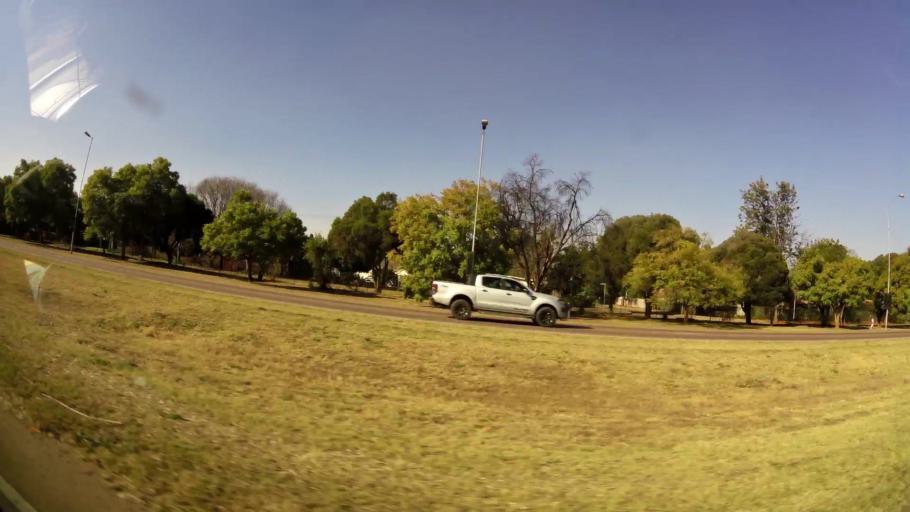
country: ZA
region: Gauteng
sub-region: City of Tshwane Metropolitan Municipality
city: Pretoria
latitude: -25.7182
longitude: 28.2578
